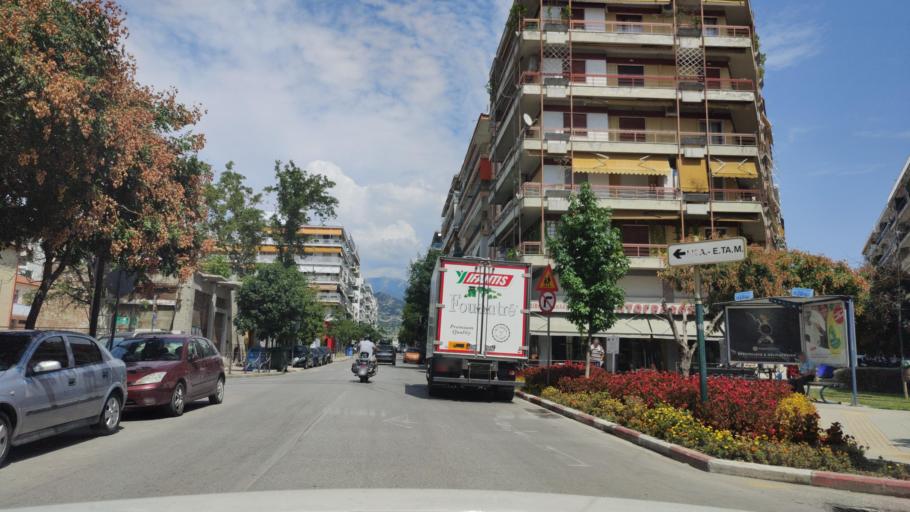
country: GR
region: Central Macedonia
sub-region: Nomos Serron
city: Serres
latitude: 41.0905
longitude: 23.5549
